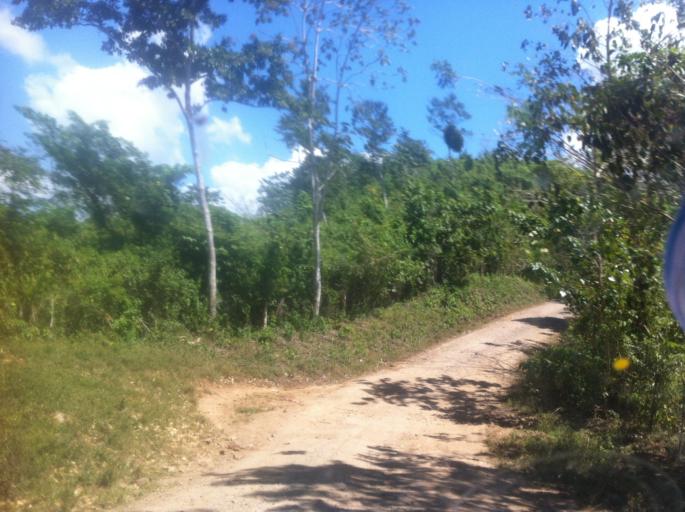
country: NI
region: Rio San Juan
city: San Carlos
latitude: 11.2389
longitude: -84.5122
